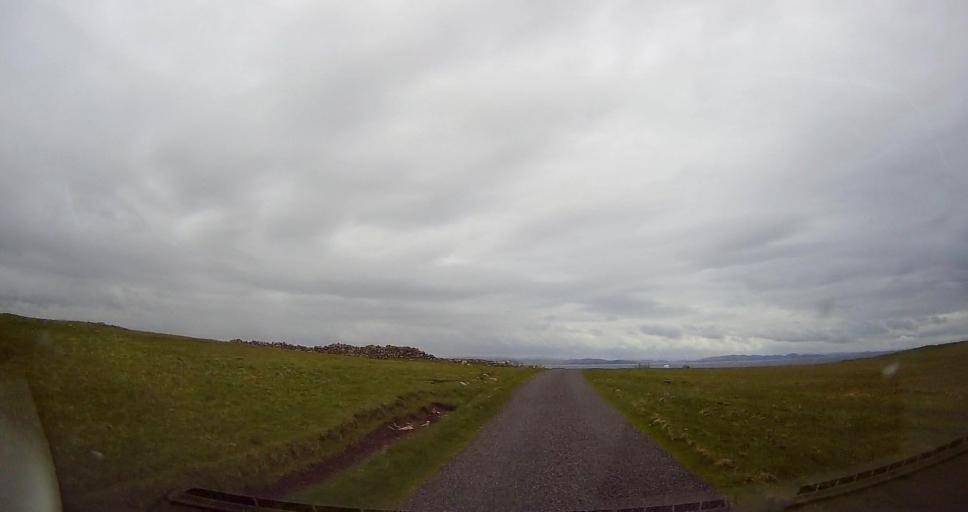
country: GB
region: Scotland
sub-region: Shetland Islands
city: Lerwick
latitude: 60.4889
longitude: -1.6185
